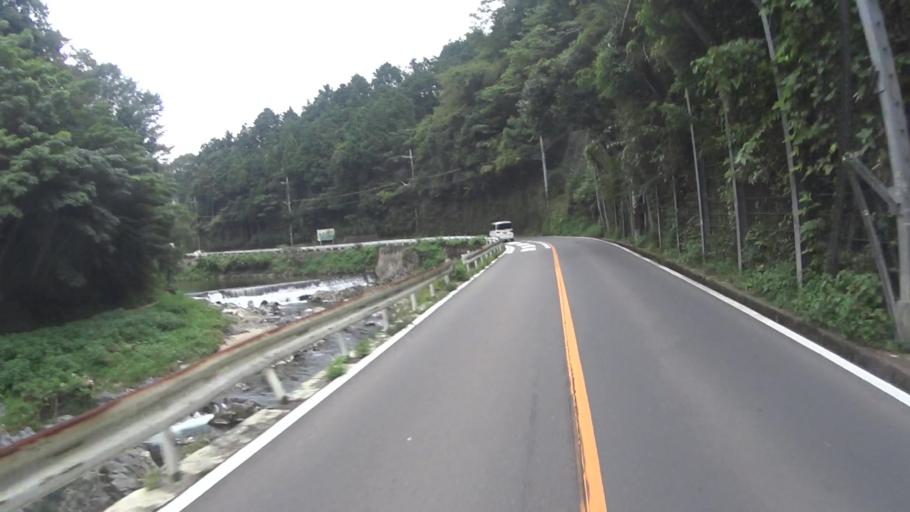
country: JP
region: Kyoto
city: Tanabe
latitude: 34.7927
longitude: 135.8988
